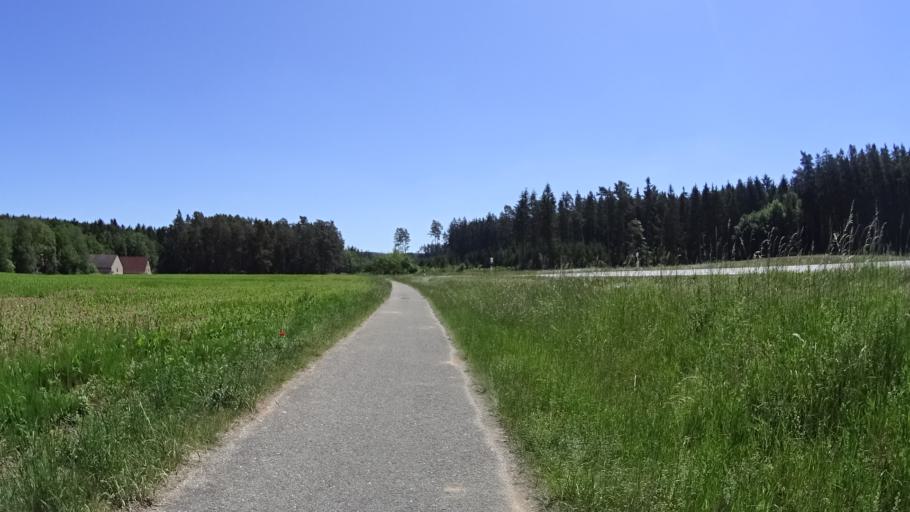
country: DE
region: Bavaria
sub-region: Regierungsbezirk Mittelfranken
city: Pleinfeld
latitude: 49.0992
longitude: 10.9596
